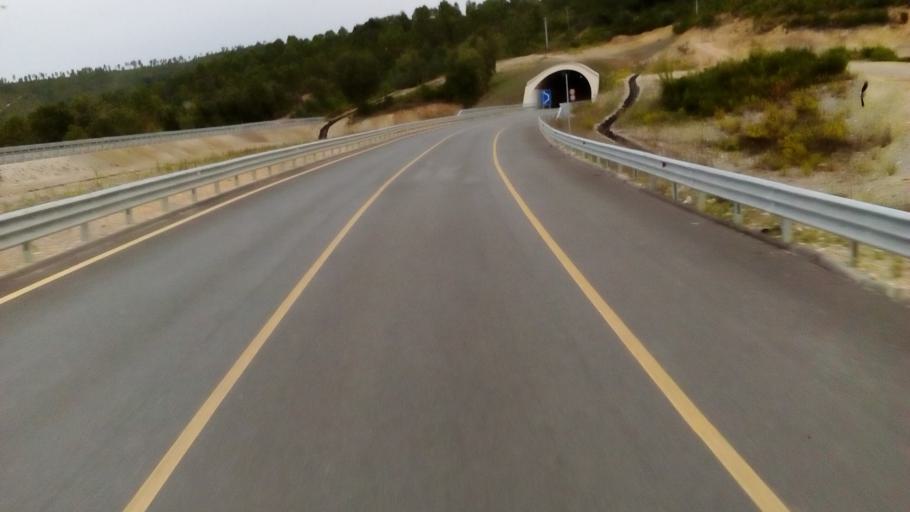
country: IT
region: Tuscany
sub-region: Provincia di Grosseto
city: Civitella Marittima
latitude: 43.0340
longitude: 11.2760
